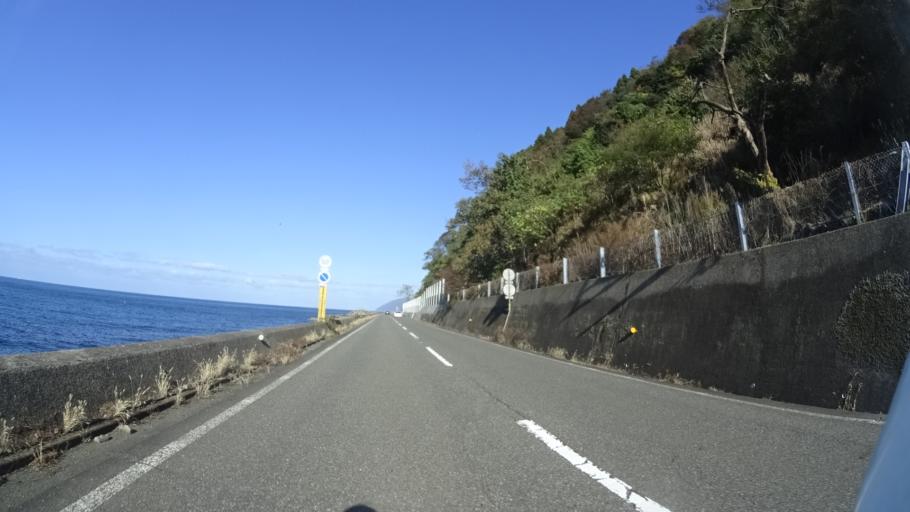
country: JP
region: Fukui
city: Tsuruga
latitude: 35.7795
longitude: 136.0998
